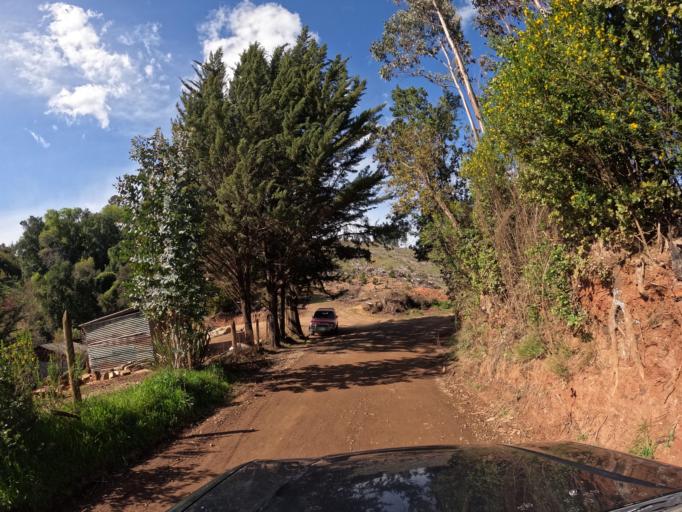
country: CL
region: Biobio
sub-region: Provincia de Concepcion
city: Chiguayante
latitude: -37.0737
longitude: -72.8391
